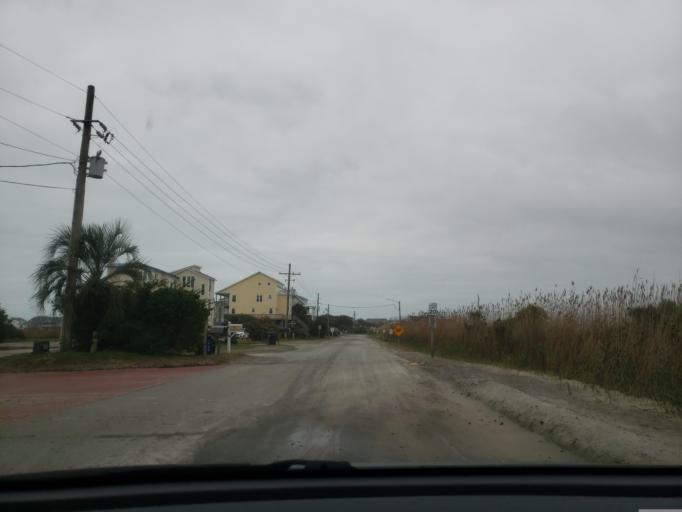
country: US
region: North Carolina
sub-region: Onslow County
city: Sneads Ferry
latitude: 34.5288
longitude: -77.3451
